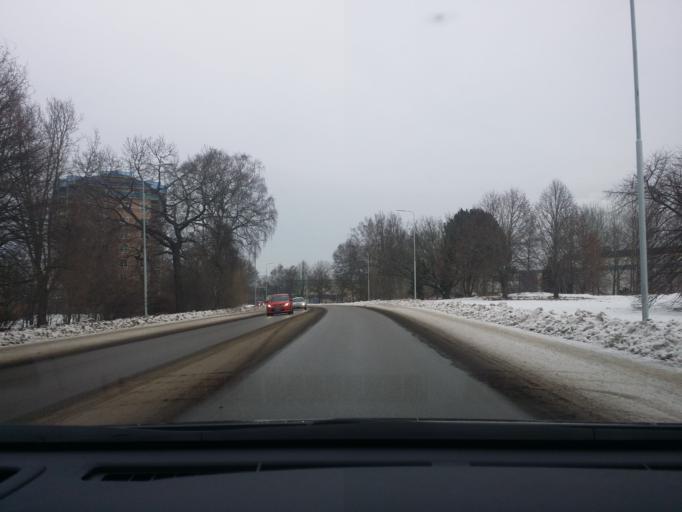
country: SE
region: Vaestra Goetaland
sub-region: Mariestads Kommun
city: Mariestad
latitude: 58.6988
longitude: 13.8188
